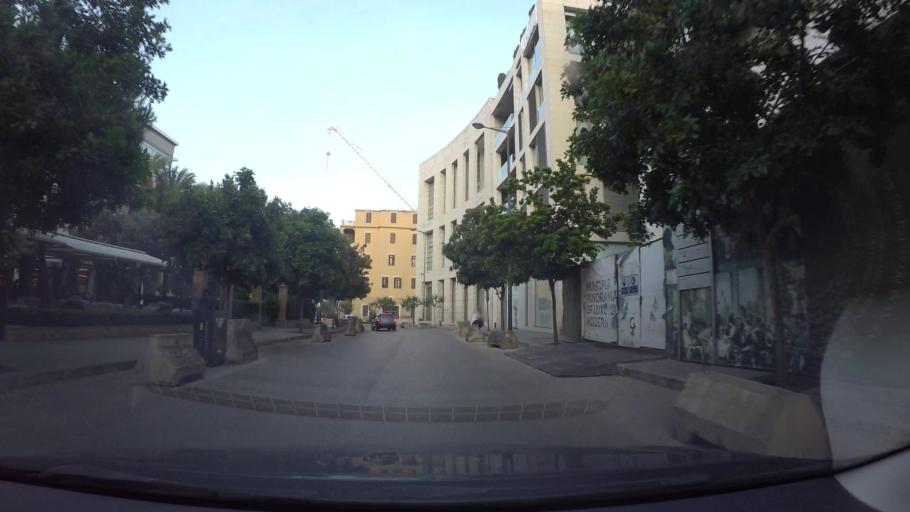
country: LB
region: Beyrouth
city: Beirut
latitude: 33.8984
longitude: 35.4996
